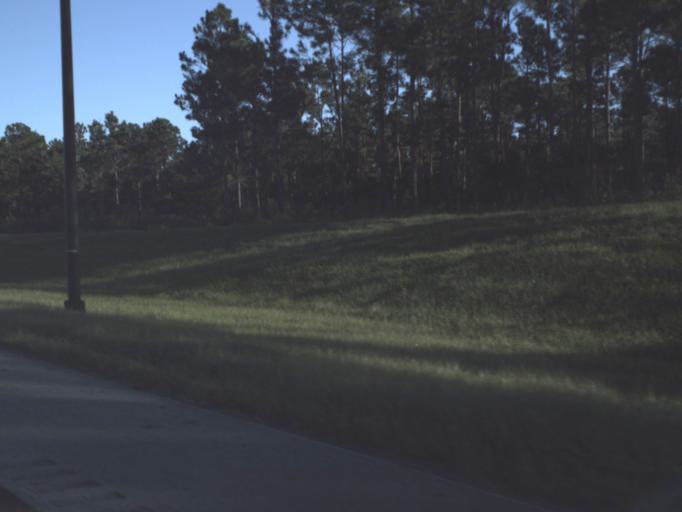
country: US
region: Florida
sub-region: Polk County
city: Citrus Ridge
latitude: 28.4023
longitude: -81.6234
